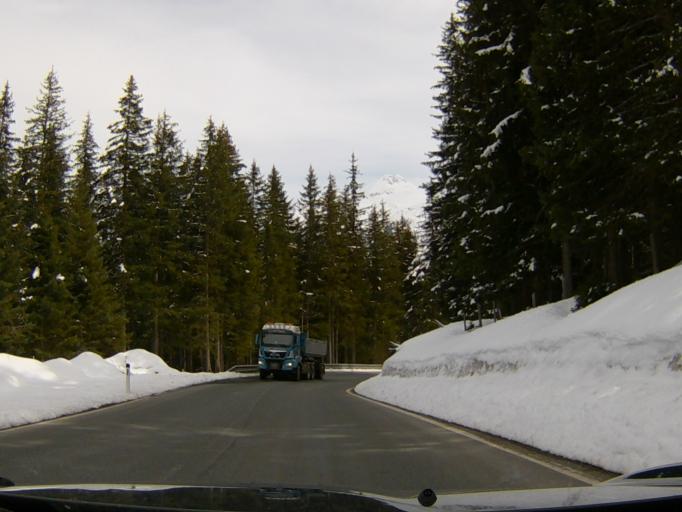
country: AT
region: Salzburg
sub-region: Politischer Bezirk Zell am See
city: Krimml
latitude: 47.2334
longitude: 12.1605
